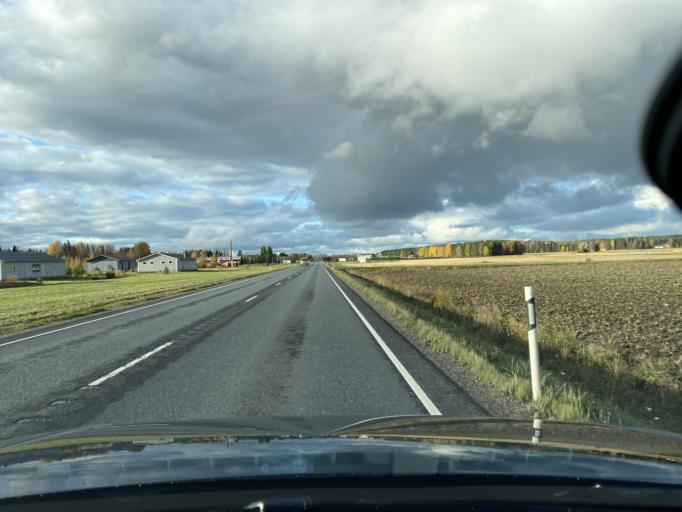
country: FI
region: Haeme
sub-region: Forssa
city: Humppila
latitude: 60.9327
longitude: 23.3774
